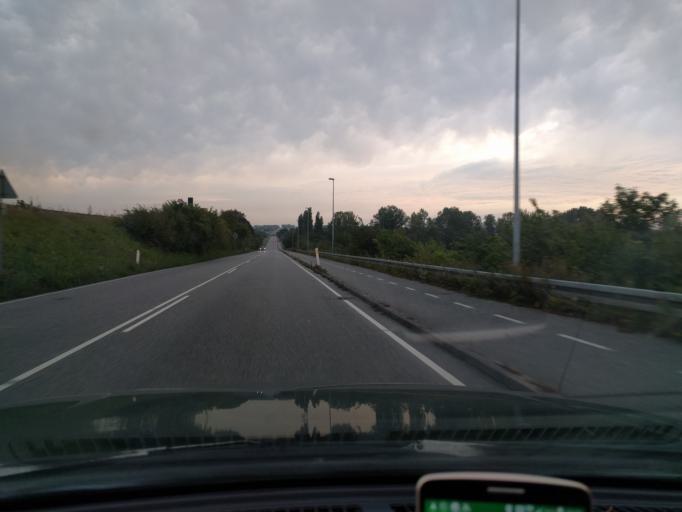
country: DK
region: Zealand
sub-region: Guldborgsund Kommune
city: Norre Alslev
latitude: 54.9523
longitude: 11.8687
